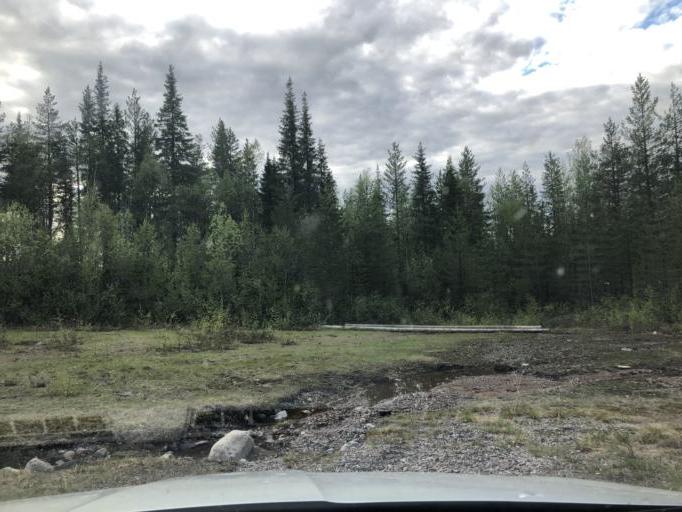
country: SE
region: Norrbotten
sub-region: Arvidsjaurs Kommun
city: Arvidsjaur
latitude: 65.6046
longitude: 19.0981
